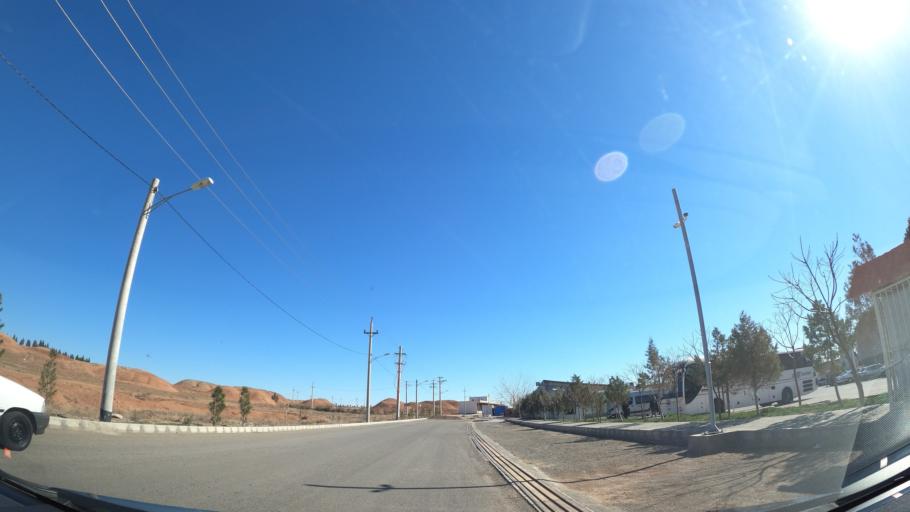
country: IR
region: Qom
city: Qom
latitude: 34.7430
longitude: 50.8678
